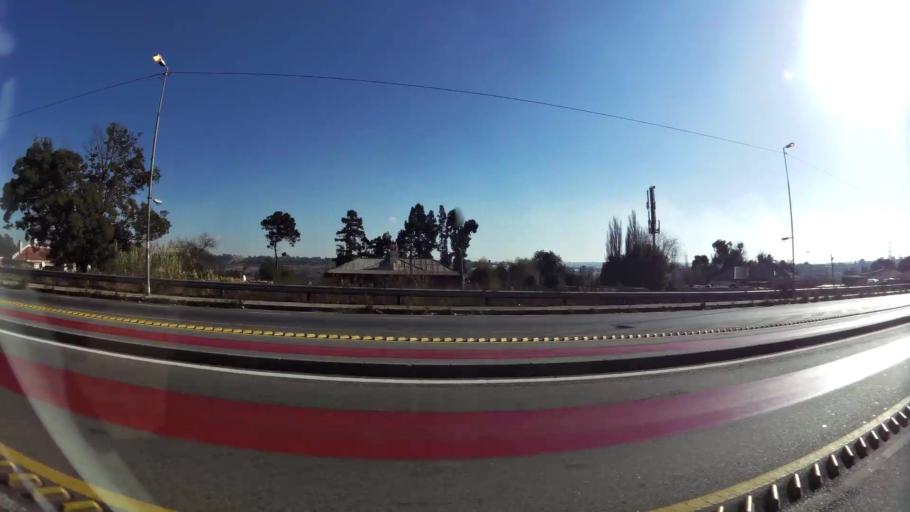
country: ZA
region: Gauteng
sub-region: City of Johannesburg Metropolitan Municipality
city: Roodepoort
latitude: -26.2152
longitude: 27.9465
